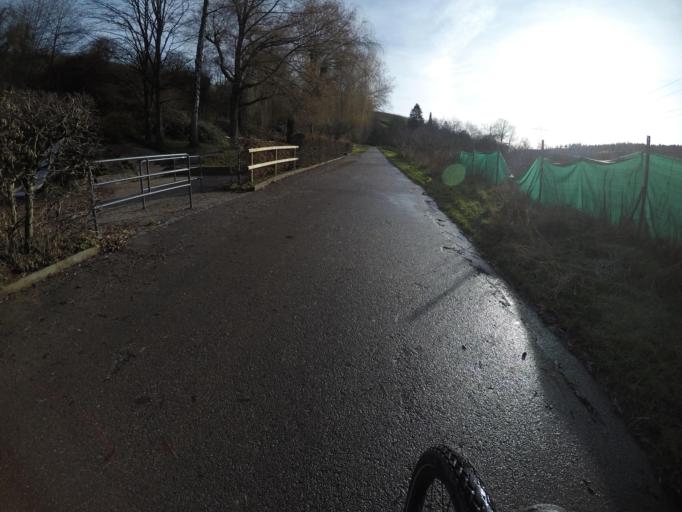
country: DE
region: Baden-Wuerttemberg
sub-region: Regierungsbezirk Stuttgart
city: Weinstadt-Endersbach
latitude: 48.7774
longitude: 9.3387
